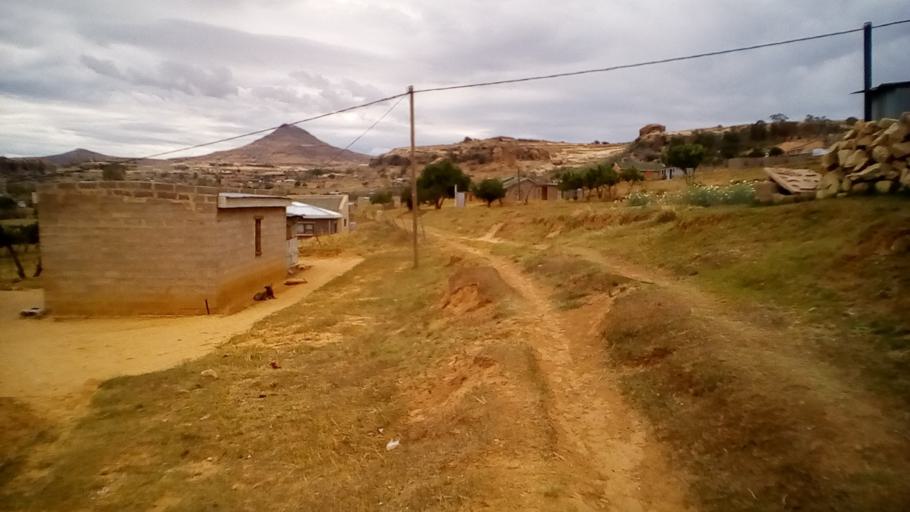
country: LS
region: Leribe
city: Leribe
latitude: -29.0238
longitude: 28.0220
